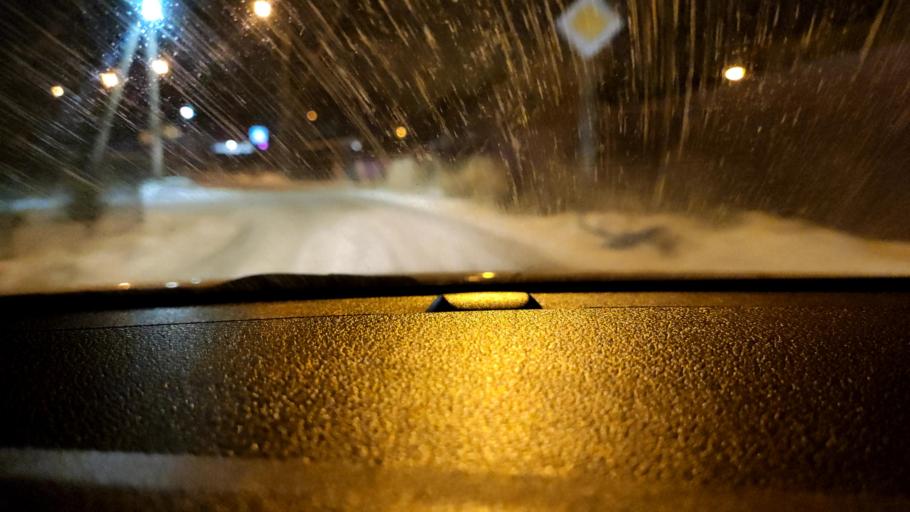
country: RU
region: Tatarstan
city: Osinovo
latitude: 55.8292
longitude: 48.8595
